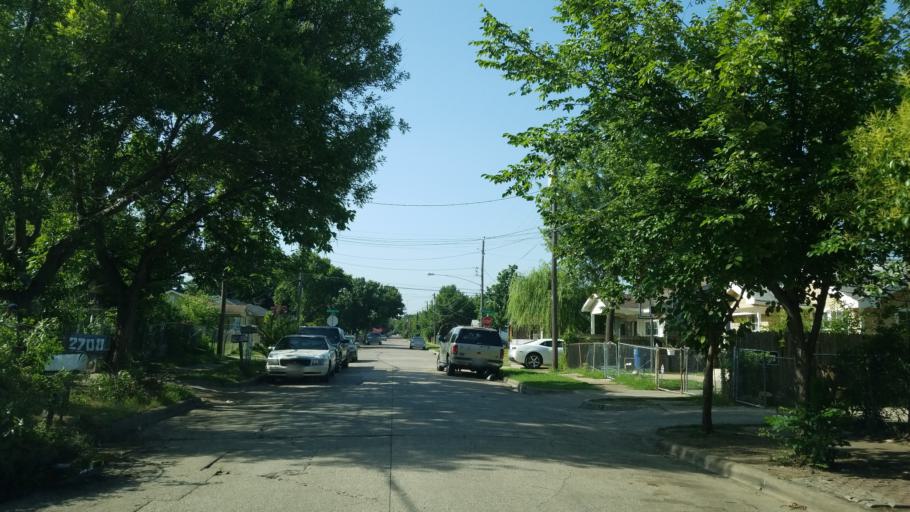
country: US
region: Texas
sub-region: Dallas County
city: Cockrell Hill
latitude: 32.7767
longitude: -96.9063
